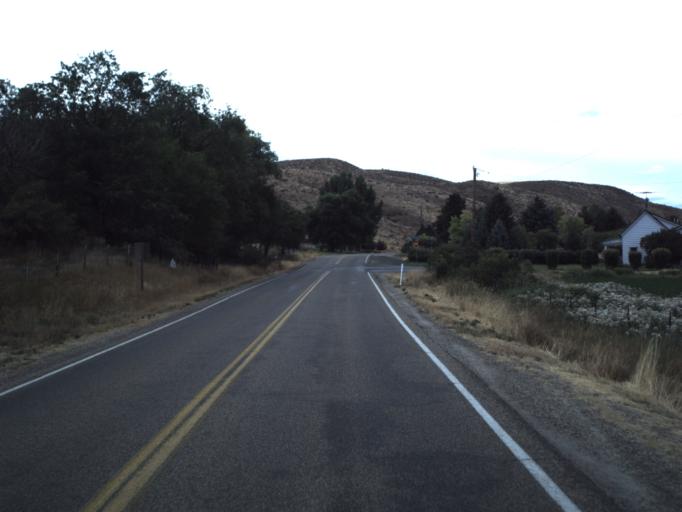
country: US
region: Utah
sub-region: Morgan County
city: Morgan
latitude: 41.0091
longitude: -111.6767
